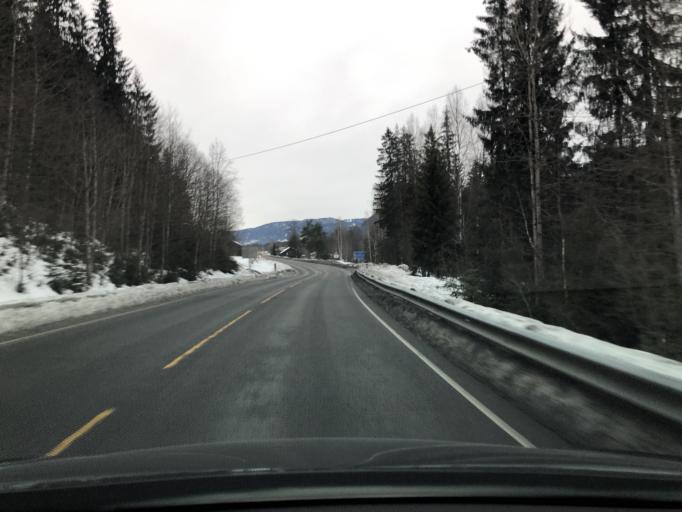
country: NO
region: Oppland
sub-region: Nordre Land
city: Dokka
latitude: 60.6095
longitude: 9.9526
